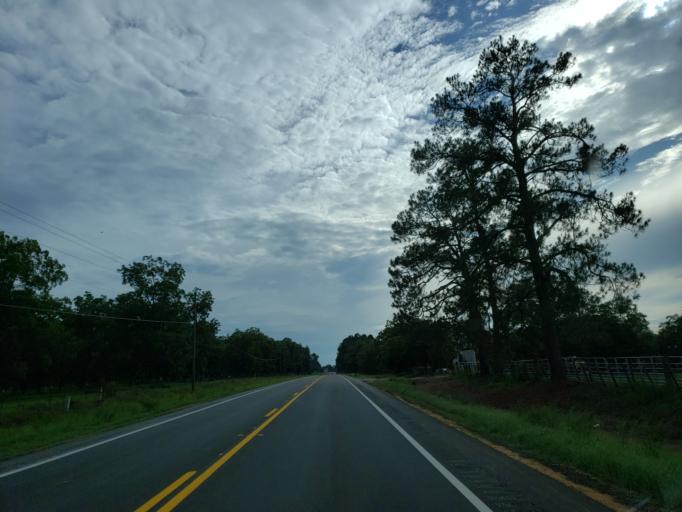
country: US
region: Georgia
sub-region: Irwin County
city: Ocilla
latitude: 31.5853
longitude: -83.2776
